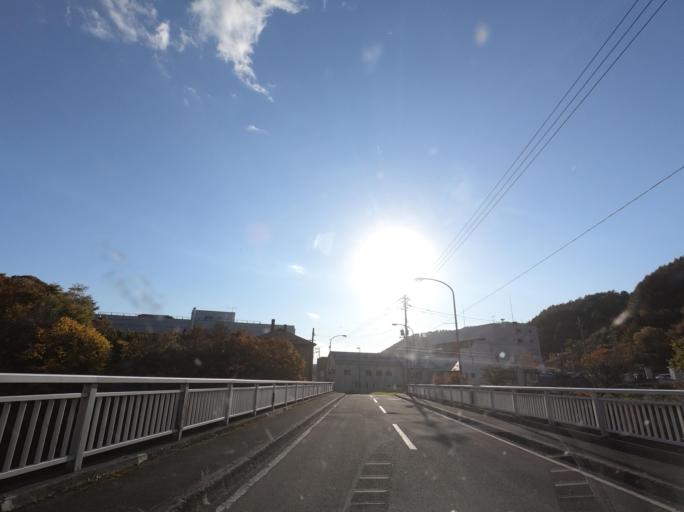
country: JP
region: Hokkaido
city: Iwamizawa
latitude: 43.0573
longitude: 141.9760
